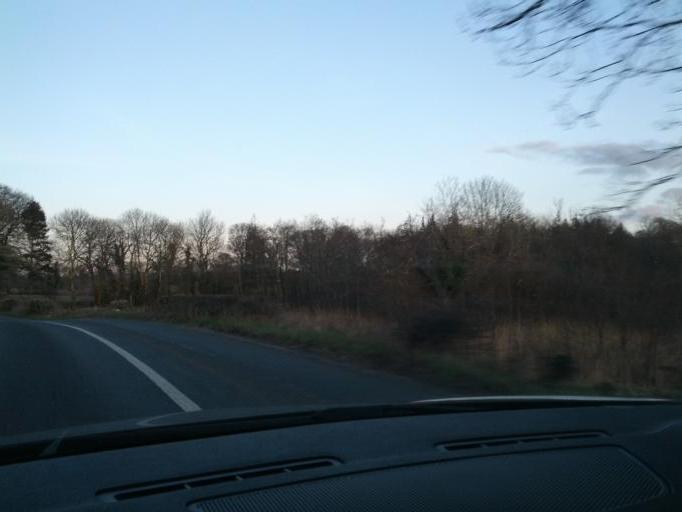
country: IE
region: Connaught
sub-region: Roscommon
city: Boyle
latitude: 53.9688
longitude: -8.3558
